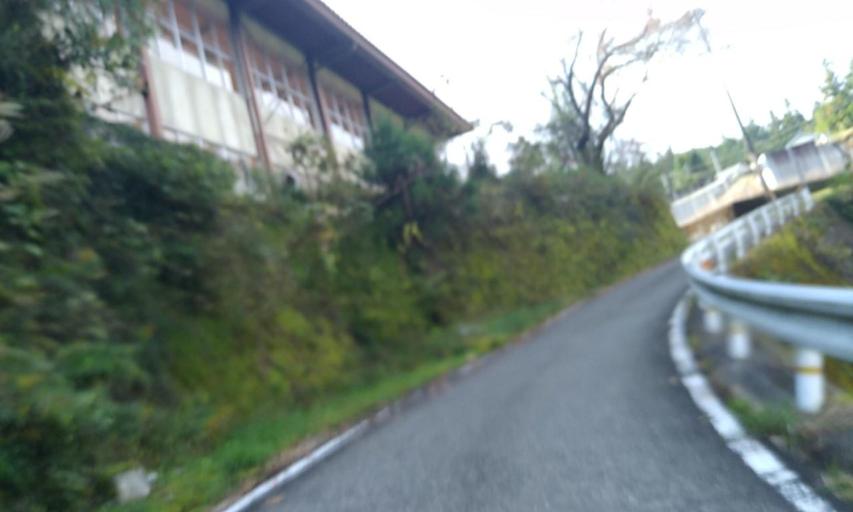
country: JP
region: Wakayama
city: Shingu
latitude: 33.9219
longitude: 135.9830
